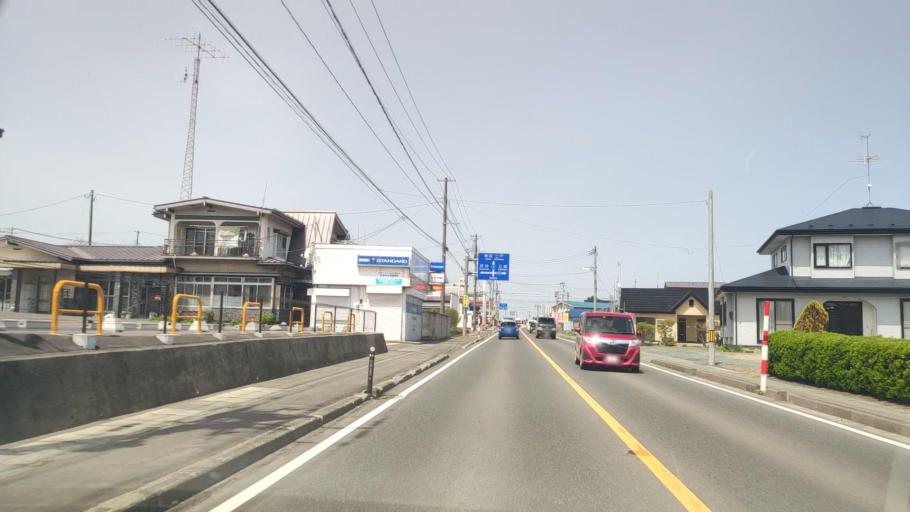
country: JP
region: Aomori
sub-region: Misawa Shi
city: Inuotose
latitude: 40.6561
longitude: 141.1931
